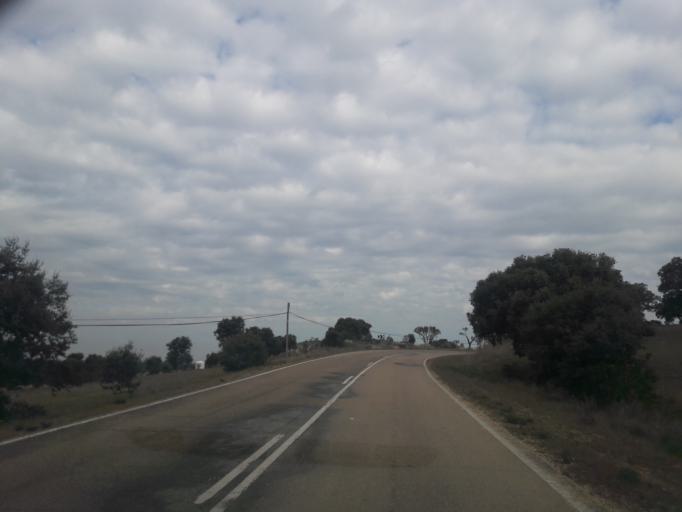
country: ES
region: Castille and Leon
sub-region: Provincia de Salamanca
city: Ciudad Rodrigo
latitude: 40.5573
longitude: -6.5294
